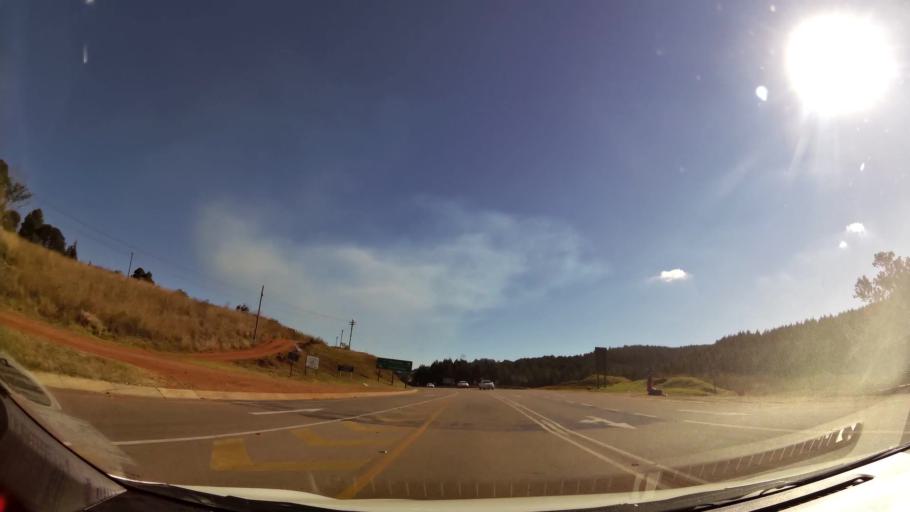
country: ZA
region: Limpopo
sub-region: Capricorn District Municipality
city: Mankoeng
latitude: -23.9399
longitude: 29.9468
